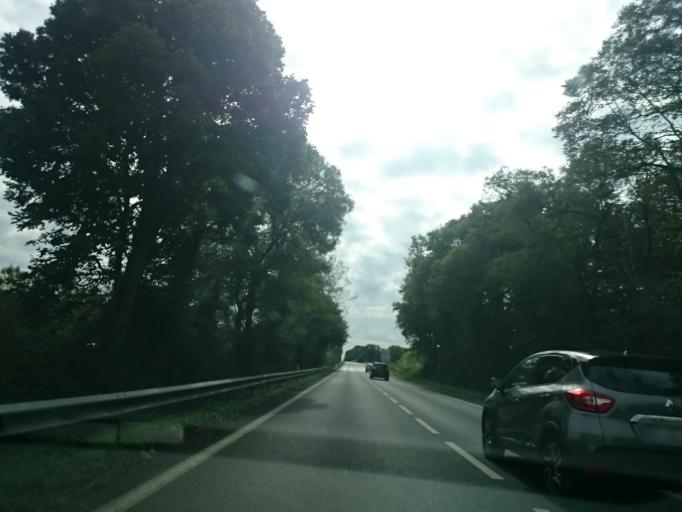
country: FR
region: Pays de la Loire
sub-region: Departement de la Loire-Atlantique
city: Vigneux-de-Bretagne
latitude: 47.2862
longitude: -1.7348
